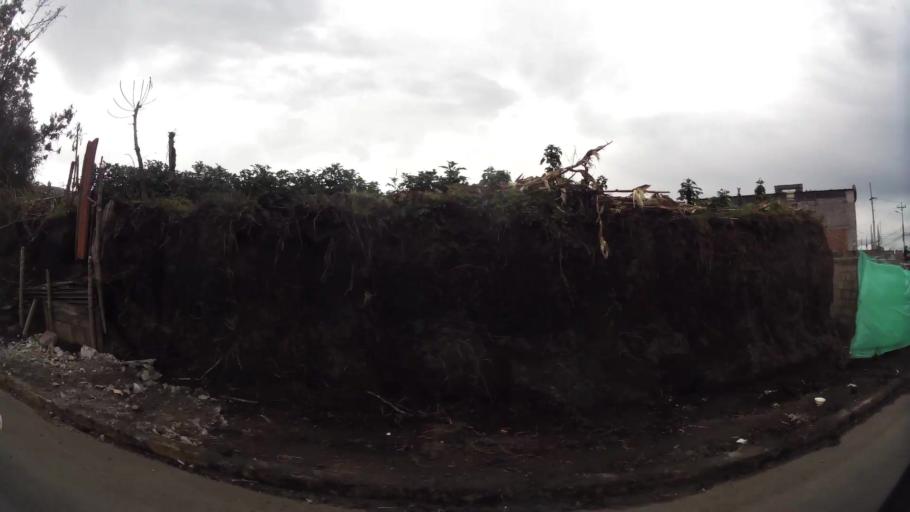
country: EC
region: Pichincha
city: Sangolqui
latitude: -0.3453
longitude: -78.5539
